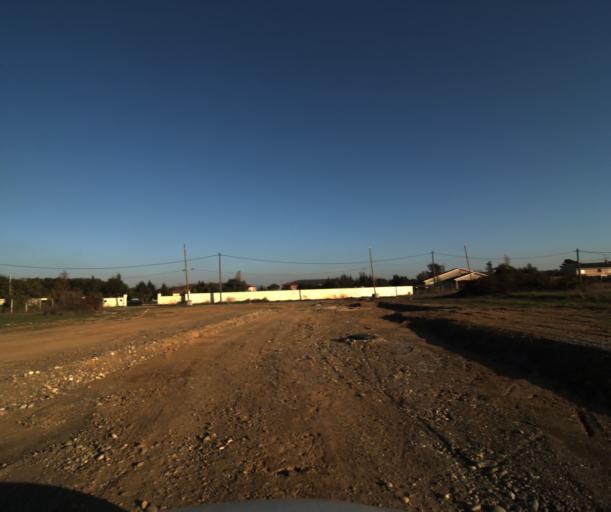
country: FR
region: Midi-Pyrenees
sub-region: Departement de la Haute-Garonne
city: Colomiers
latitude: 43.6241
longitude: 1.3386
